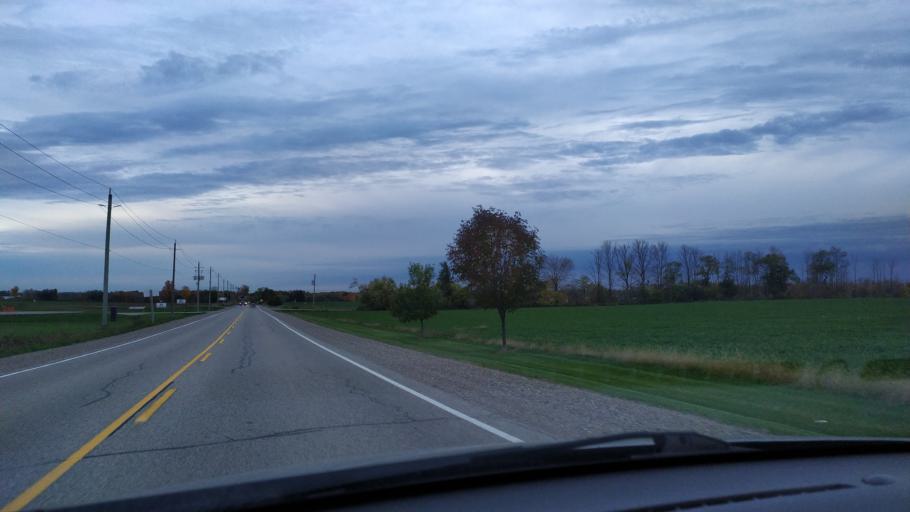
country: CA
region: Ontario
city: Stratford
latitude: 43.4781
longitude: -80.7804
